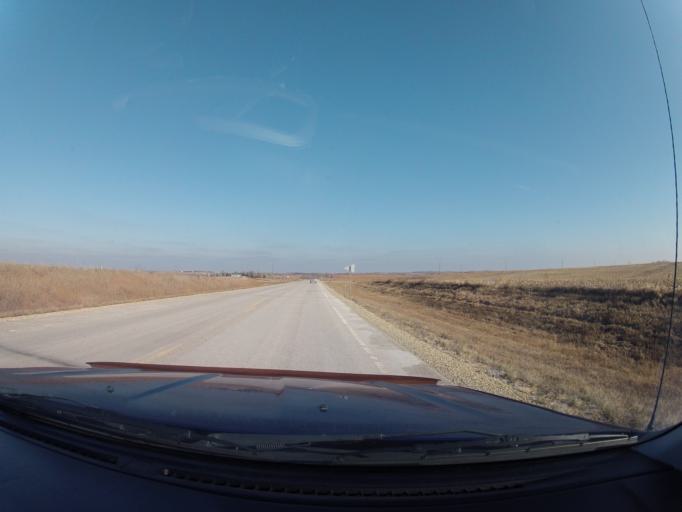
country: US
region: Kansas
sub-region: Marshall County
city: Blue Rapids
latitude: 39.5649
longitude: -96.7538
